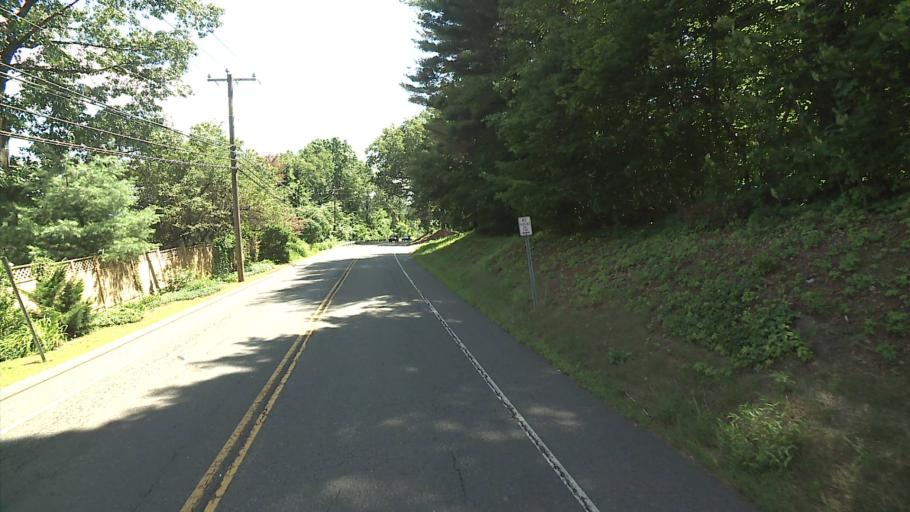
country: US
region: Massachusetts
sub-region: Hampden County
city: Southwick
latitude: 41.9968
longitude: -72.7238
